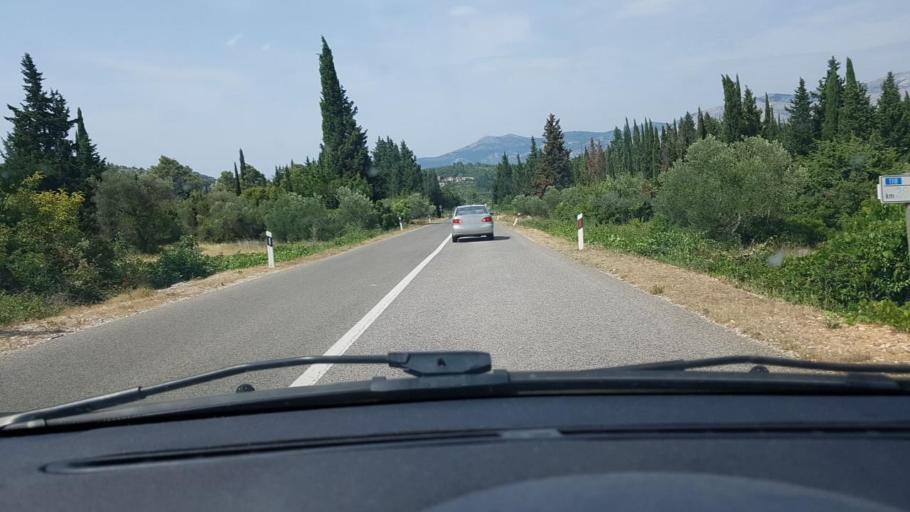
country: HR
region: Dubrovacko-Neretvanska
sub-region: Grad Korcula
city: Zrnovo
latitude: 42.9401
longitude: 17.1046
